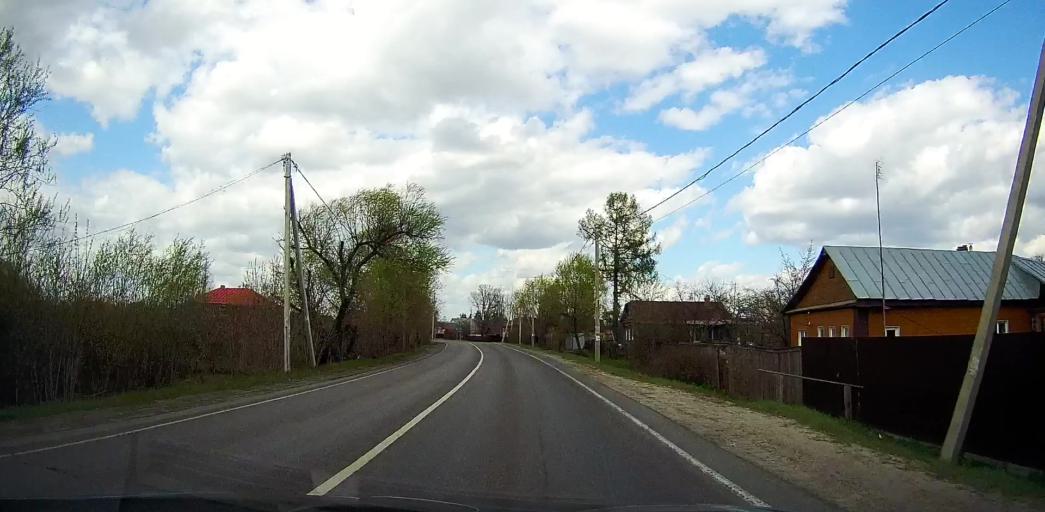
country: RU
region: Moskovskaya
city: Davydovo
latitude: 55.6334
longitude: 38.8689
